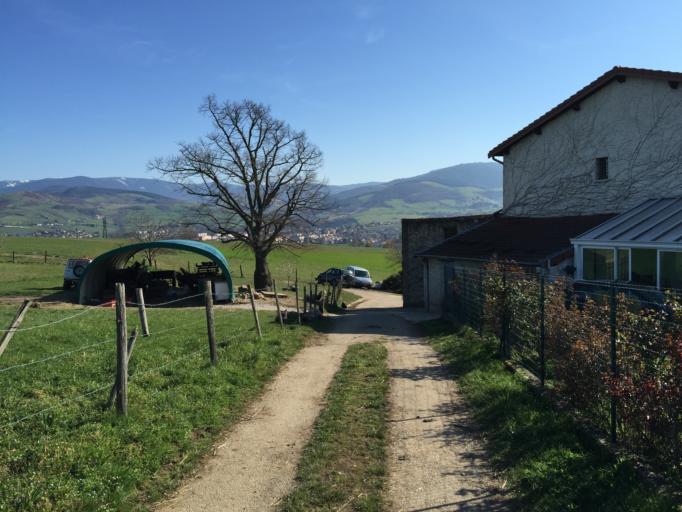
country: FR
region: Rhone-Alpes
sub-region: Departement de la Loire
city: Saint-Chamond
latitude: 45.4814
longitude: 4.4969
